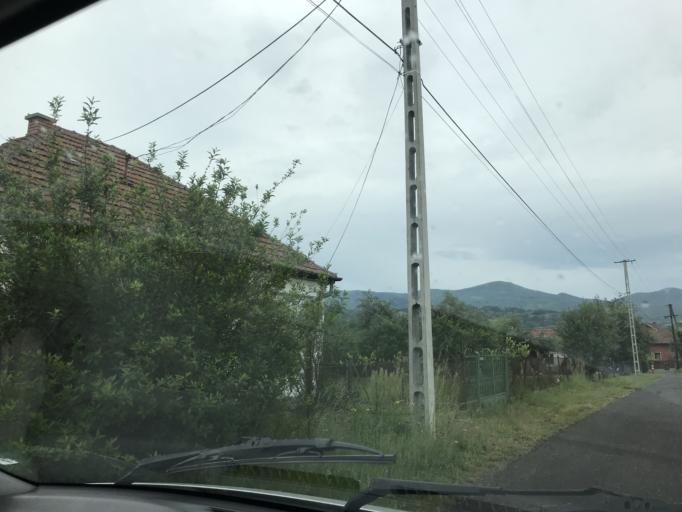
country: HU
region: Nograd
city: Batonyterenye
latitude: 47.9703
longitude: 19.8169
